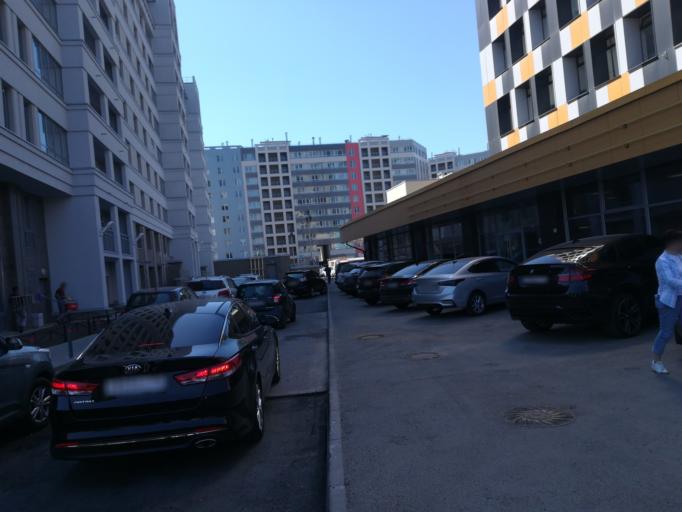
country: RU
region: St.-Petersburg
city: Vasyl'evsky Ostrov
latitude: 59.9494
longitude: 30.2675
